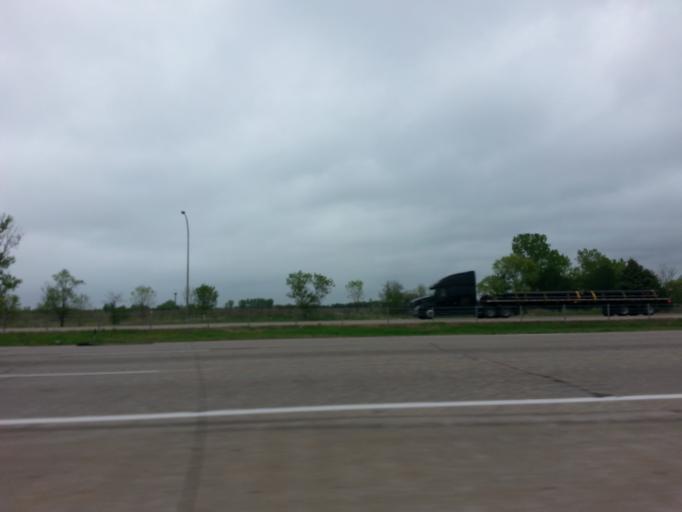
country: US
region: Minnesota
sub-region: Washington County
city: Lake Elmo
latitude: 44.9484
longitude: -92.8678
